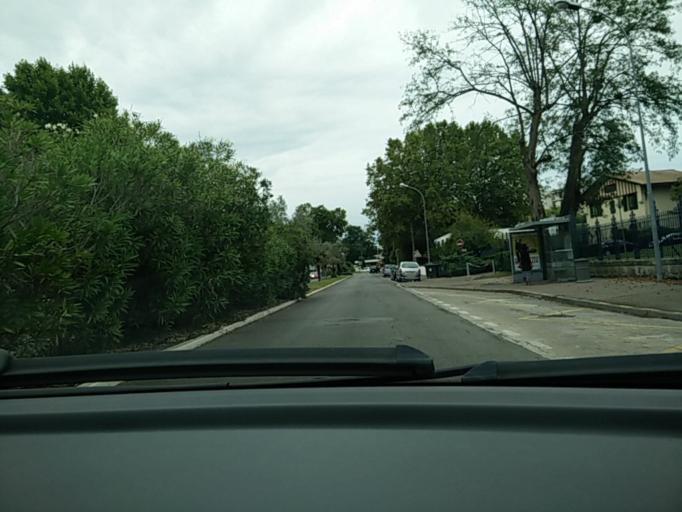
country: FR
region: Aquitaine
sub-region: Departement de la Gironde
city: Bruges
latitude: 44.8694
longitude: -0.6101
